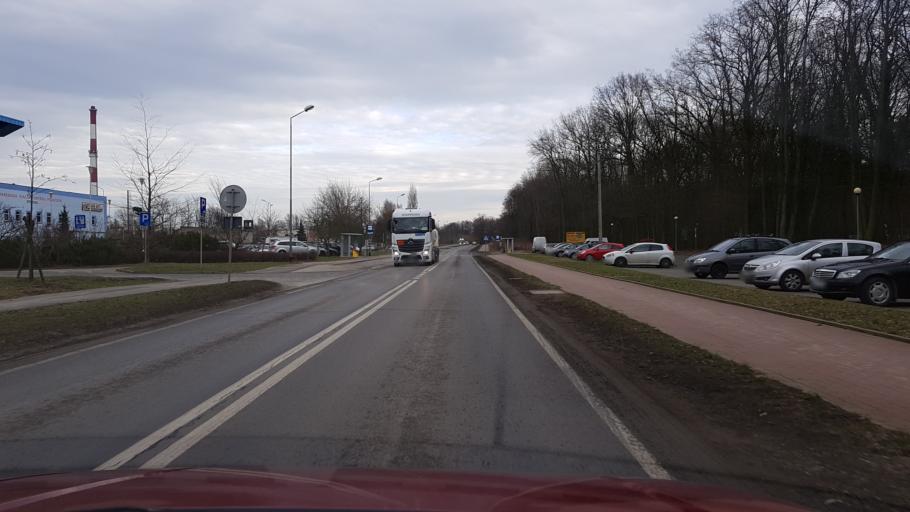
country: PL
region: West Pomeranian Voivodeship
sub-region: Powiat policki
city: Police
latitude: 53.5510
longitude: 14.5528
